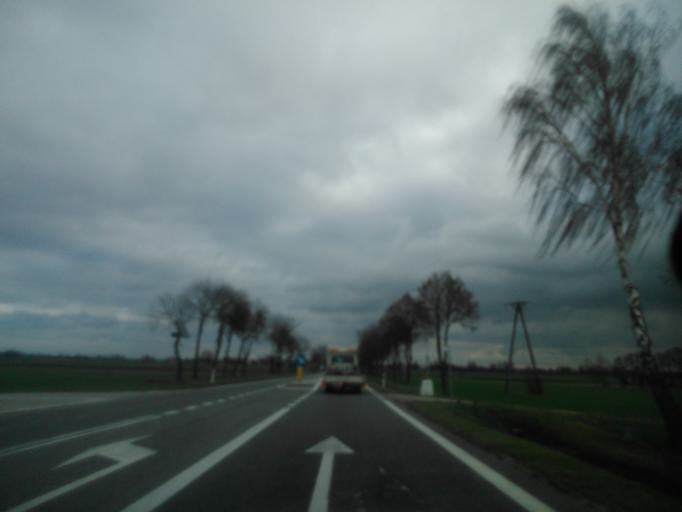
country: PL
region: Masovian Voivodeship
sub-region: Powiat plonski
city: Dzierzaznia
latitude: 52.6326
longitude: 20.1735
